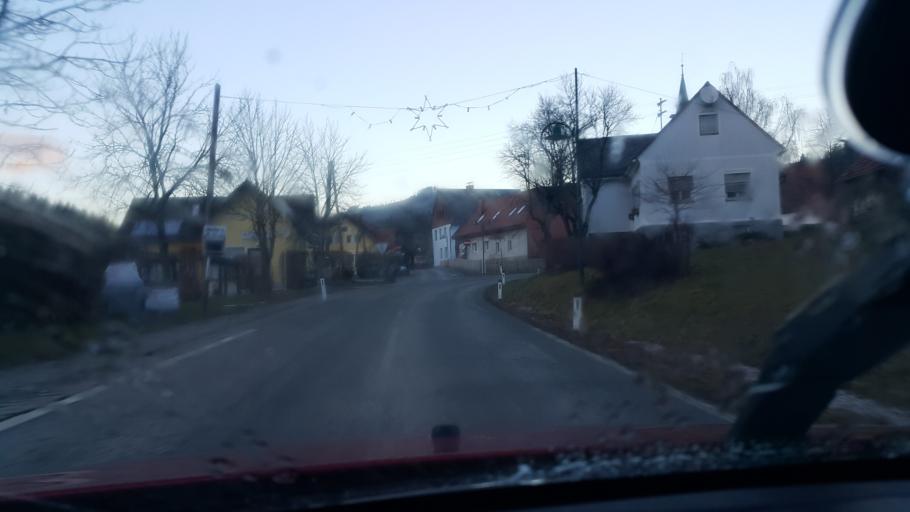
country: AT
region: Styria
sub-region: Politischer Bezirk Graz-Umgebung
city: Stiwoll
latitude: 47.1016
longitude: 15.2188
